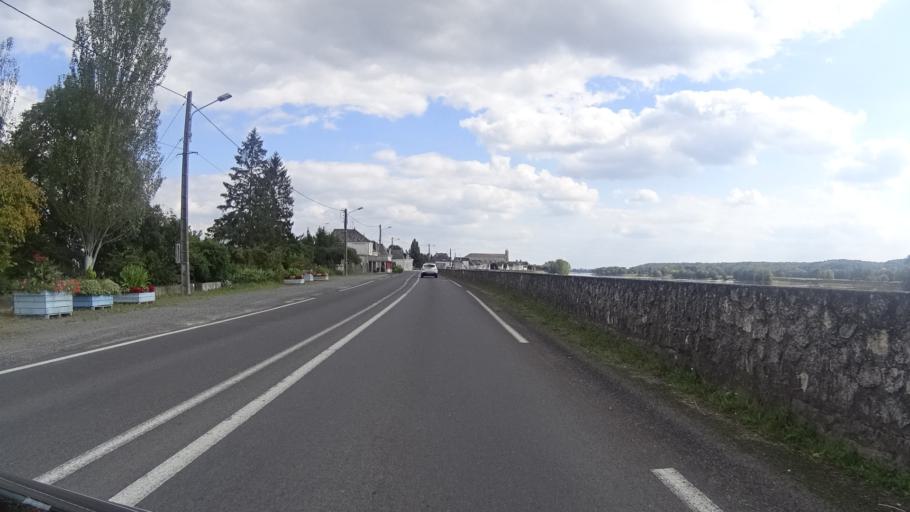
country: FR
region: Pays de la Loire
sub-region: Departement de Maine-et-Loire
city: Saint-Clement-des-Levees
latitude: 47.3343
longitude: -0.1932
